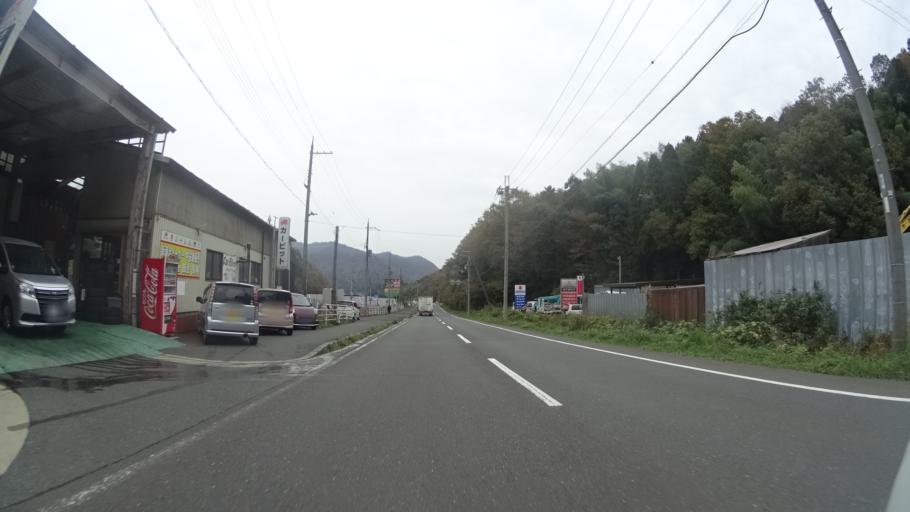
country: JP
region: Kyoto
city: Maizuru
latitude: 35.4702
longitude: 135.4241
